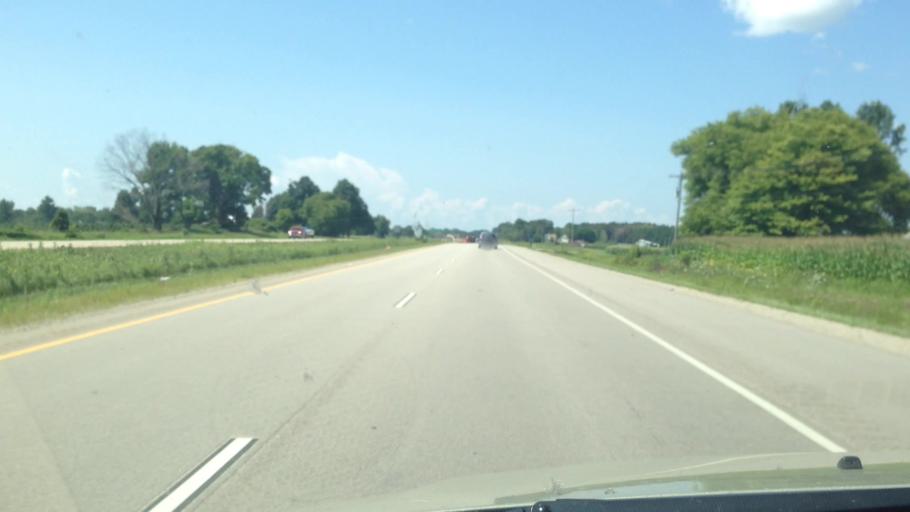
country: US
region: Wisconsin
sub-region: Oconto County
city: Oconto Falls
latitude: 44.7993
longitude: -88.0226
